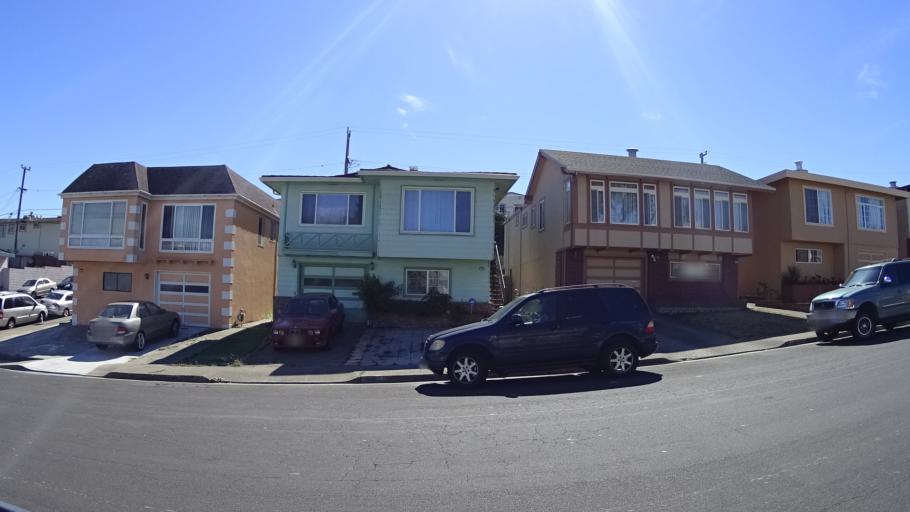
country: US
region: California
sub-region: San Mateo County
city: Broadmoor
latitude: 37.6741
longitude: -122.4813
